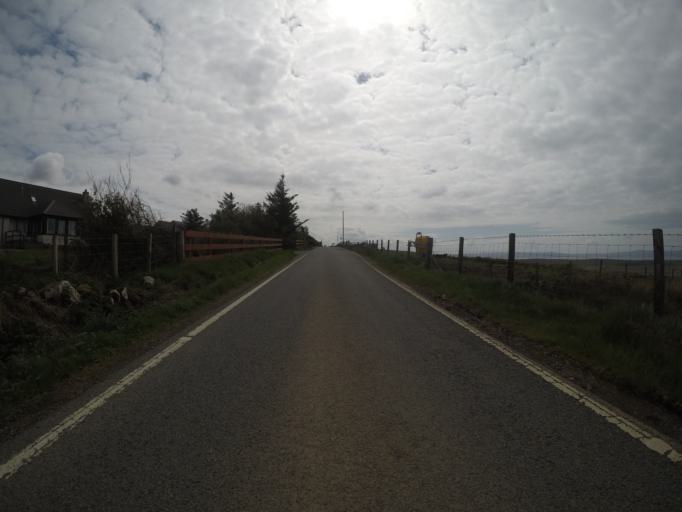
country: GB
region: Scotland
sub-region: Highland
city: Portree
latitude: 57.6401
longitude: -6.3765
